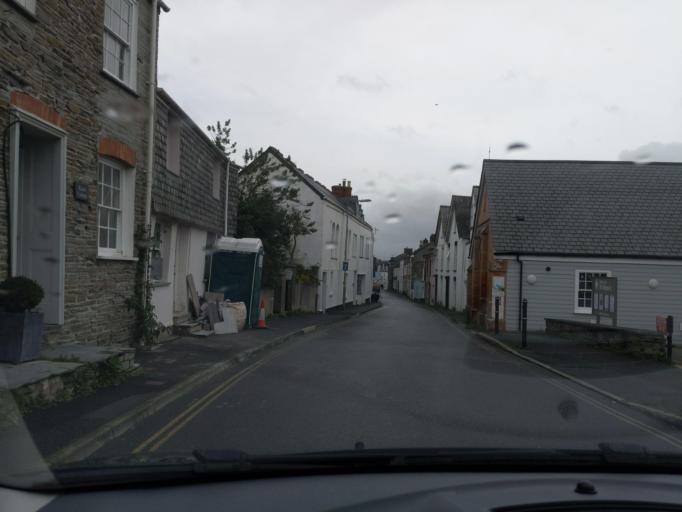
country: GB
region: England
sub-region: Cornwall
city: Padstow
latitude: 50.5415
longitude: -4.9427
